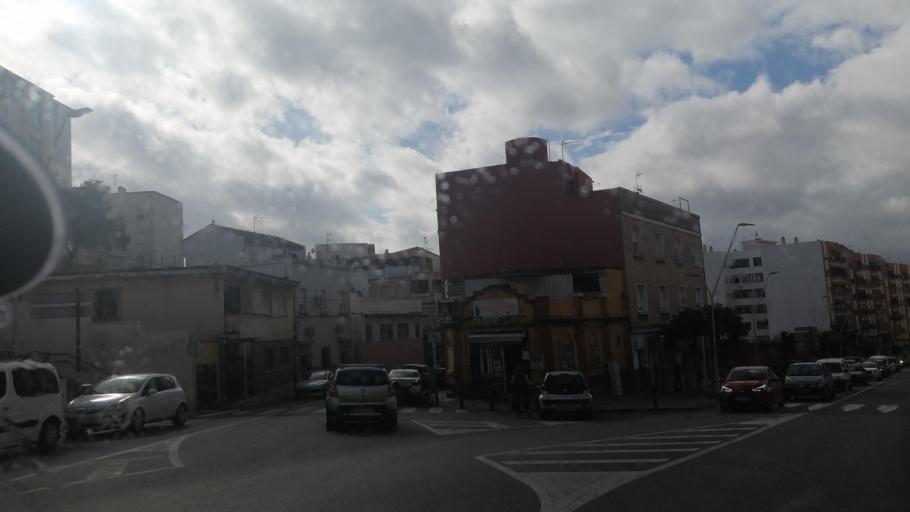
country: ES
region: Ceuta
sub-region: Ceuta
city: Ceuta
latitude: 35.8832
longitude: -5.3282
